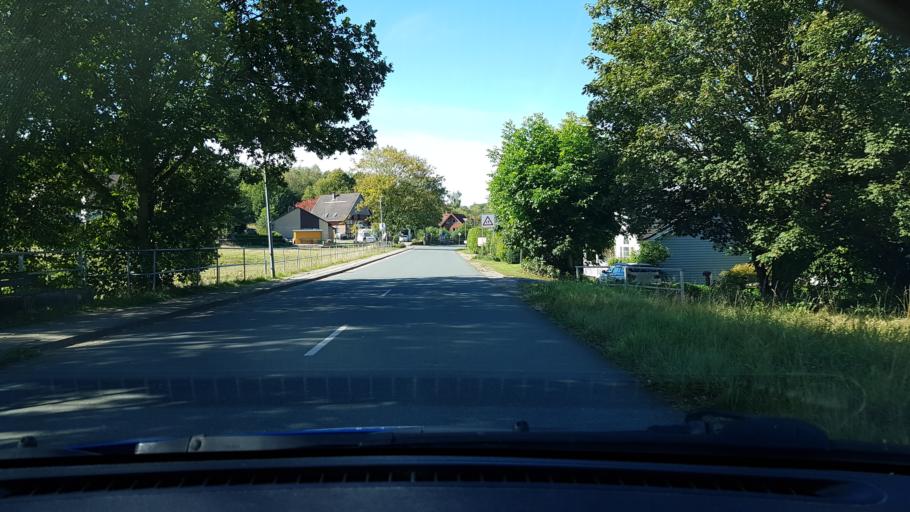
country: DE
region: Lower Saxony
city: Barsinghausen
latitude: 52.2585
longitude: 9.4472
